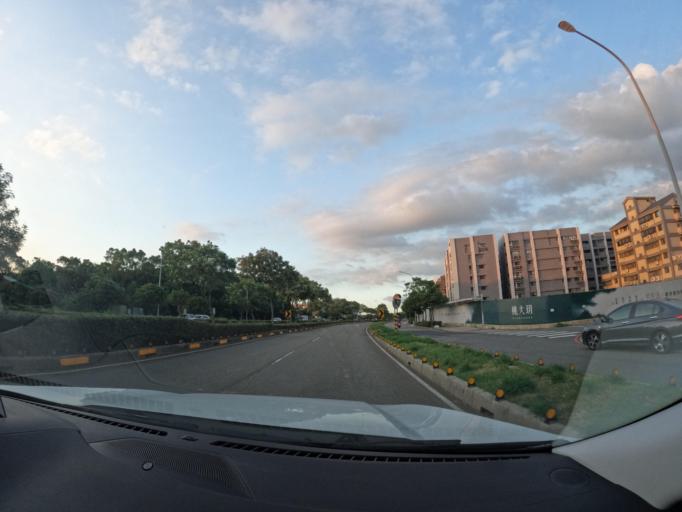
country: TW
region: Taiwan
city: Taoyuan City
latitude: 25.0221
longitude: 121.2155
